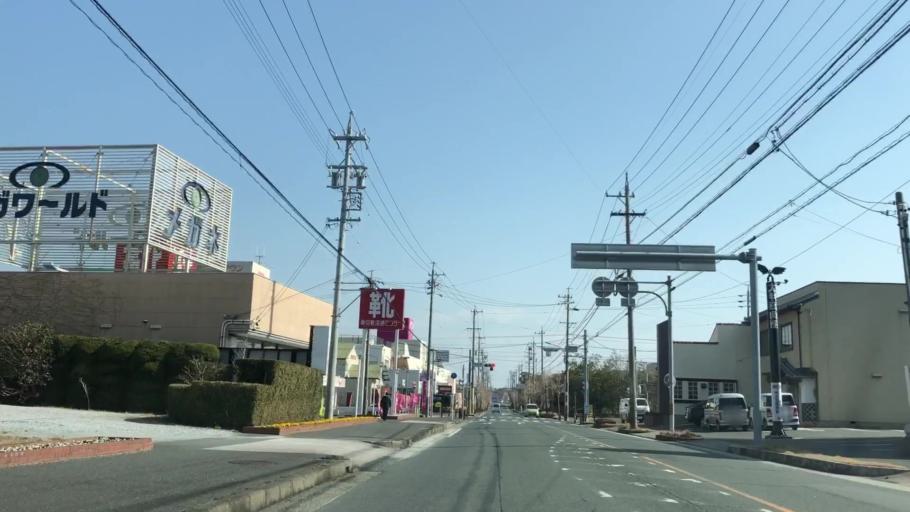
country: JP
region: Aichi
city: Tahara
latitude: 34.6735
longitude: 137.2724
